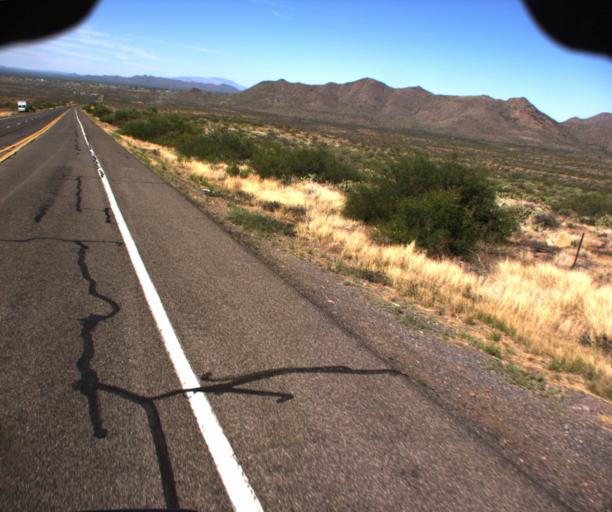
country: US
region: Arizona
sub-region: Yavapai County
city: Congress
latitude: 34.2061
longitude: -112.8026
